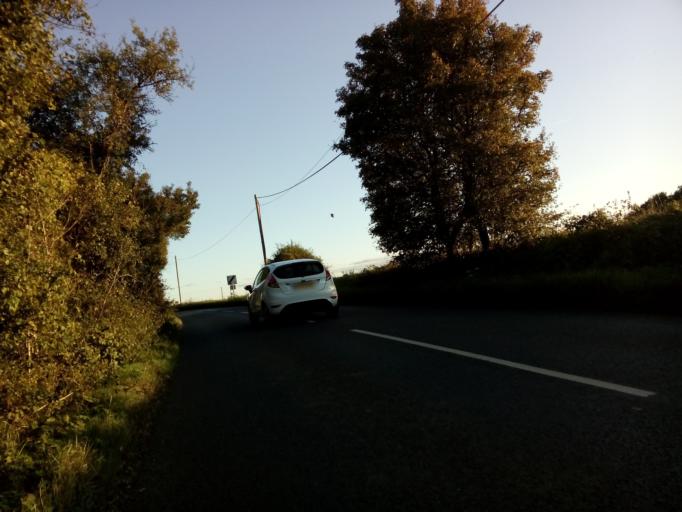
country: GB
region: England
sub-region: Suffolk
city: Sudbury
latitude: 52.0097
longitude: 0.7503
